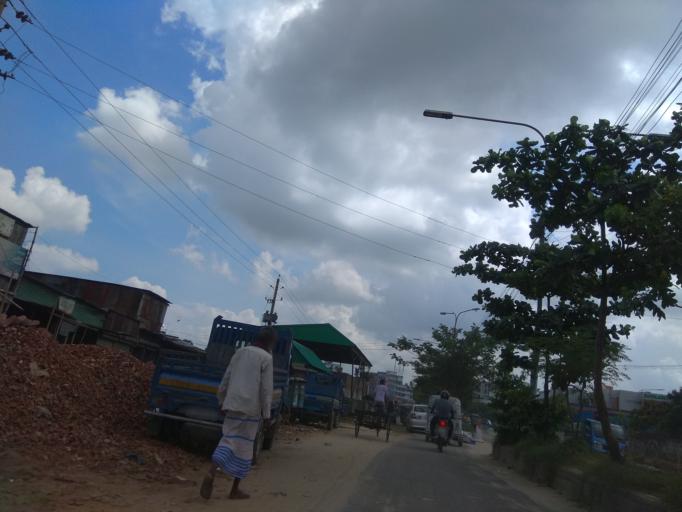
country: BD
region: Dhaka
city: Paltan
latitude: 23.8104
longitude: 90.3919
